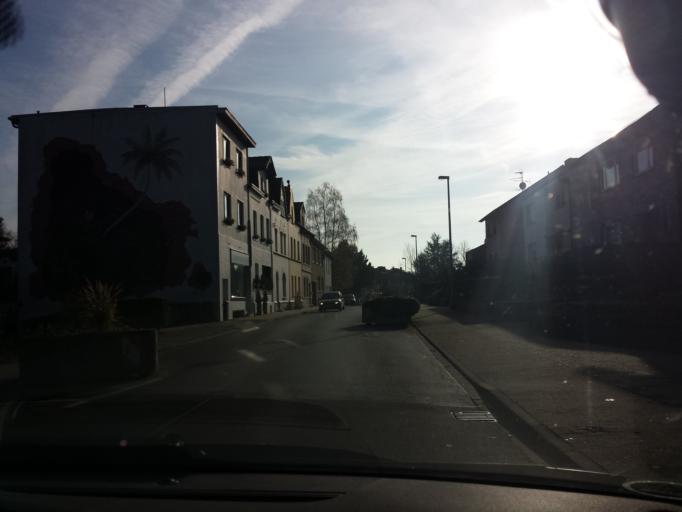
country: DE
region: North Rhine-Westphalia
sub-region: Regierungsbezirk Koln
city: Herzogenrath
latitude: 50.8709
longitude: 6.0892
